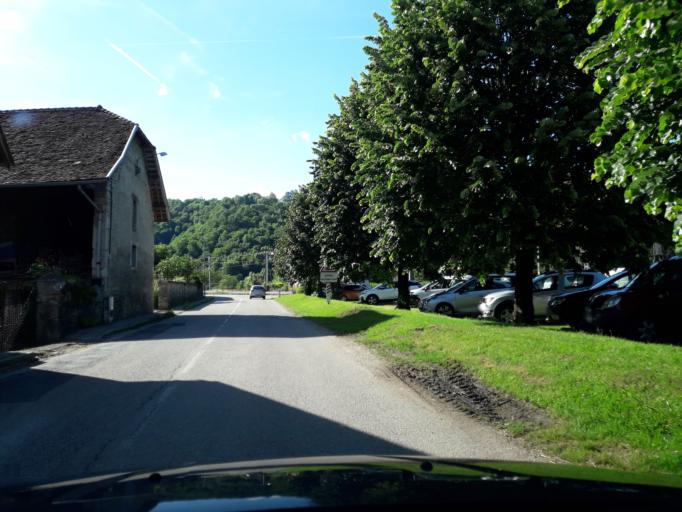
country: FR
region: Rhone-Alpes
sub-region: Departement de la Savoie
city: La Bridoire
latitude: 45.5415
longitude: 5.7622
